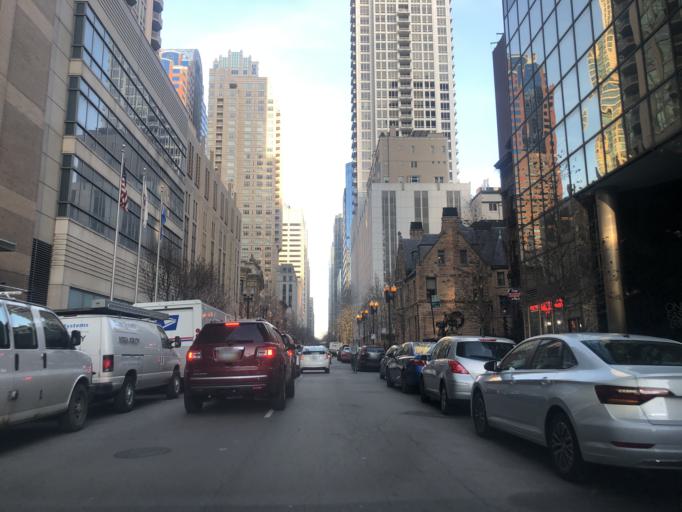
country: US
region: Illinois
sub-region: Cook County
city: Chicago
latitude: 41.8940
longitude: -87.6279
